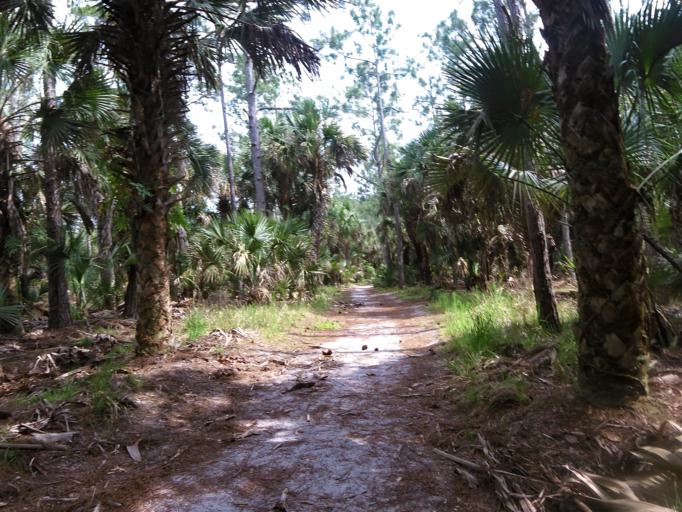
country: US
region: Florida
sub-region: Flagler County
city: Flagler Beach
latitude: 29.4033
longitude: -81.1224
